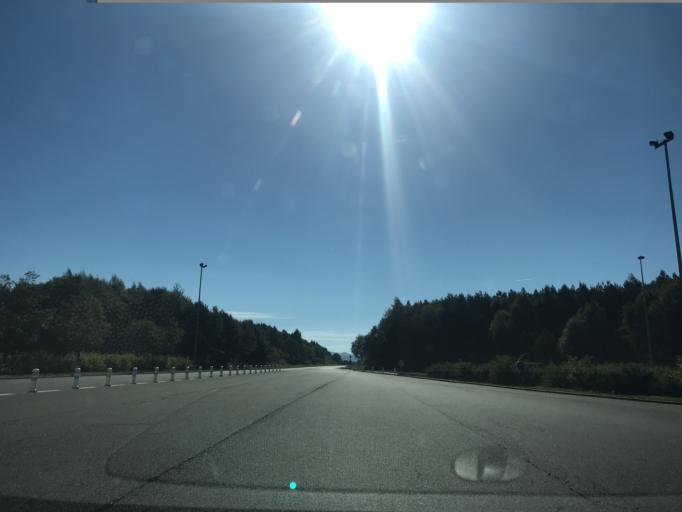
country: FR
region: Auvergne
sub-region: Departement du Puy-de-Dome
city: Saint-Sauves-d'Auvergne
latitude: 45.6659
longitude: 2.6826
